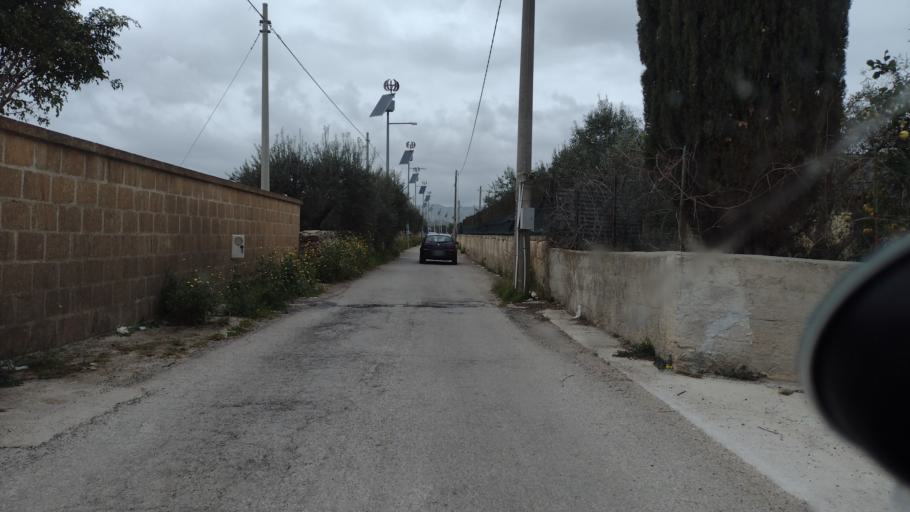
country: IT
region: Sicily
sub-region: Provincia di Siracusa
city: Avola
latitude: 36.8894
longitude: 15.1195
